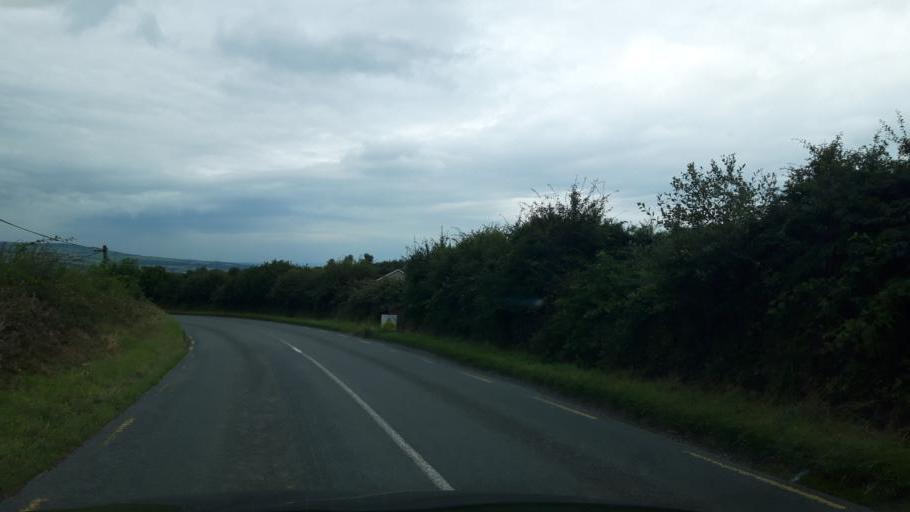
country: IE
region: Leinster
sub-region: Kilkenny
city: Ballyragget
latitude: 52.8012
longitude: -7.2996
